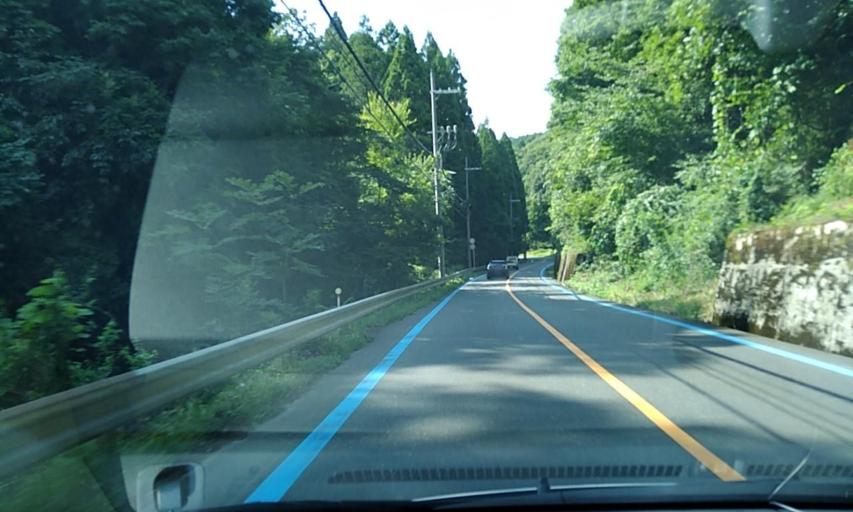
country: JP
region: Kyoto
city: Ayabe
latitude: 35.3050
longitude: 135.2950
